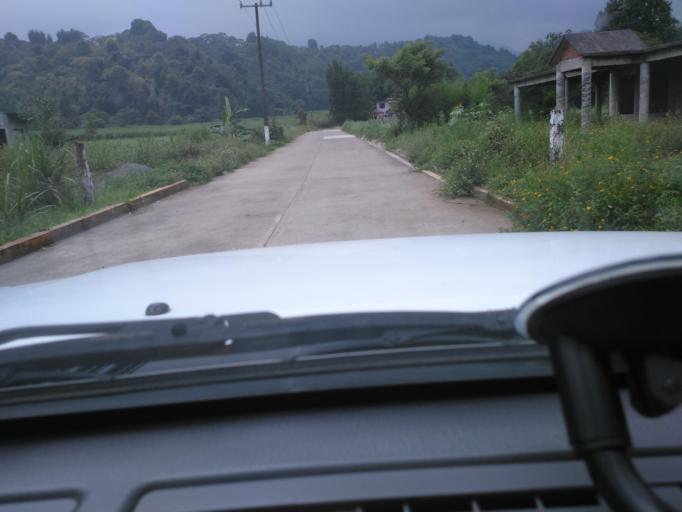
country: MX
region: Veracruz
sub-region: Mariano Escobedo
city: Chicola
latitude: 18.9097
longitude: -97.1084
